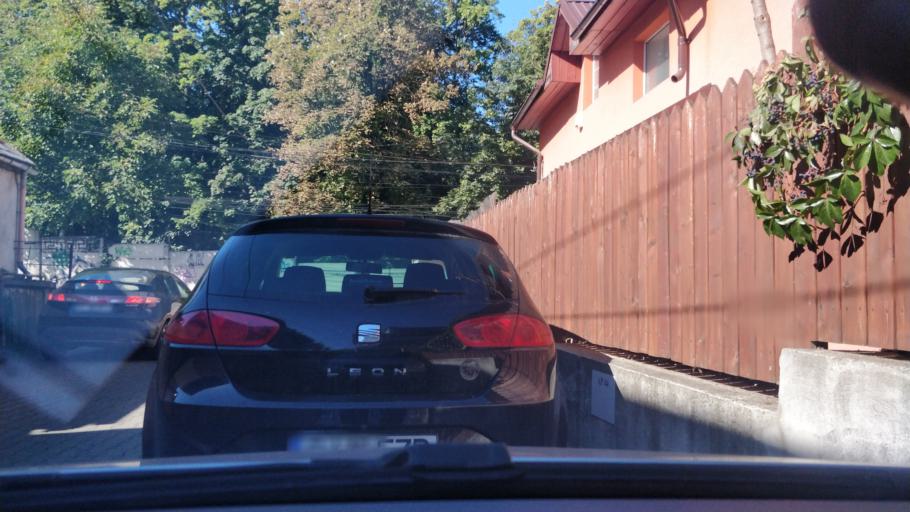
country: RO
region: Cluj
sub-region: Municipiul Cluj-Napoca
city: Cluj-Napoca
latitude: 46.7623
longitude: 23.5735
